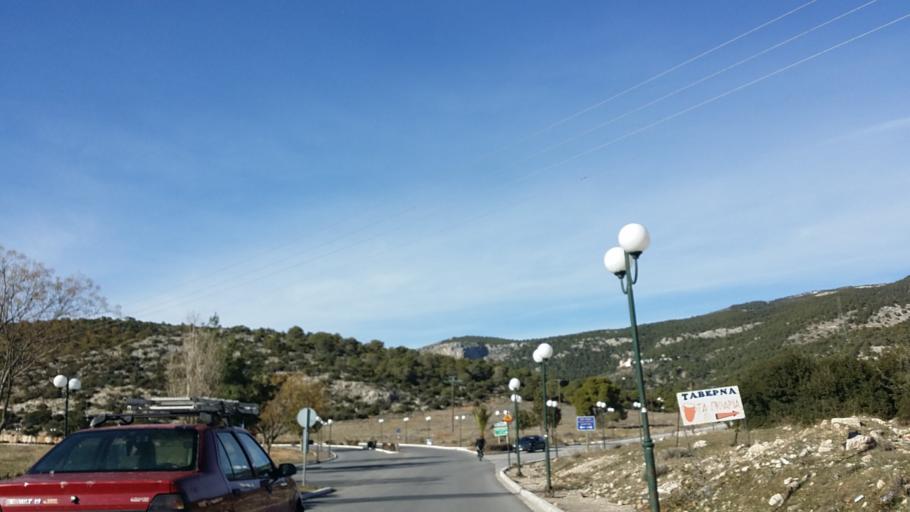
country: GR
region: Attica
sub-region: Nomarchia Dytikis Attikis
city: Fyli
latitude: 38.0985
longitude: 23.6817
